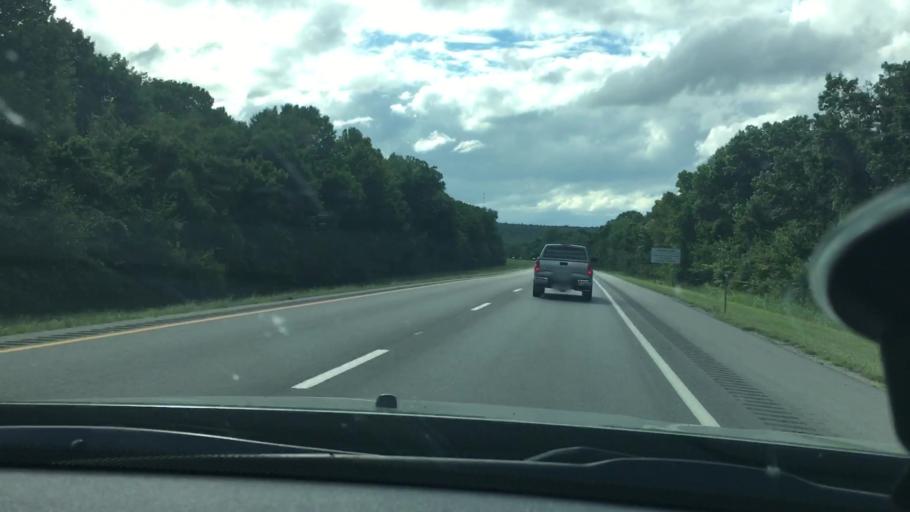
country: US
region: Oklahoma
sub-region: Okmulgee County
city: Morris
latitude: 35.4509
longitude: -95.7443
